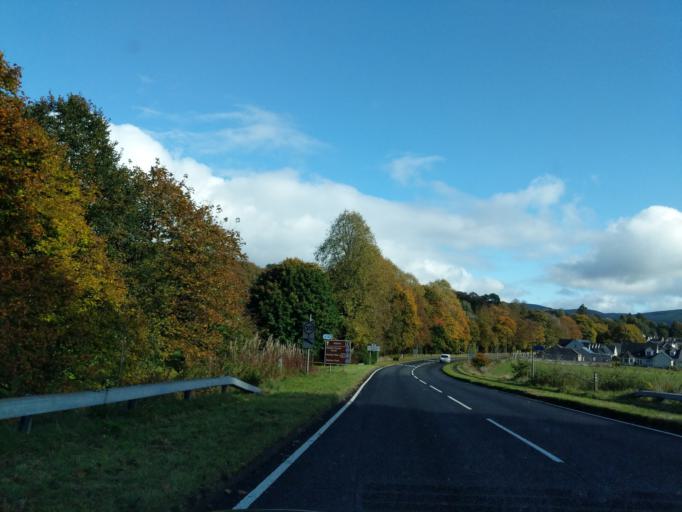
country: GB
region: Scotland
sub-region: Dumfries and Galloway
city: Moffat
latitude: 55.3372
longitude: -3.4527
